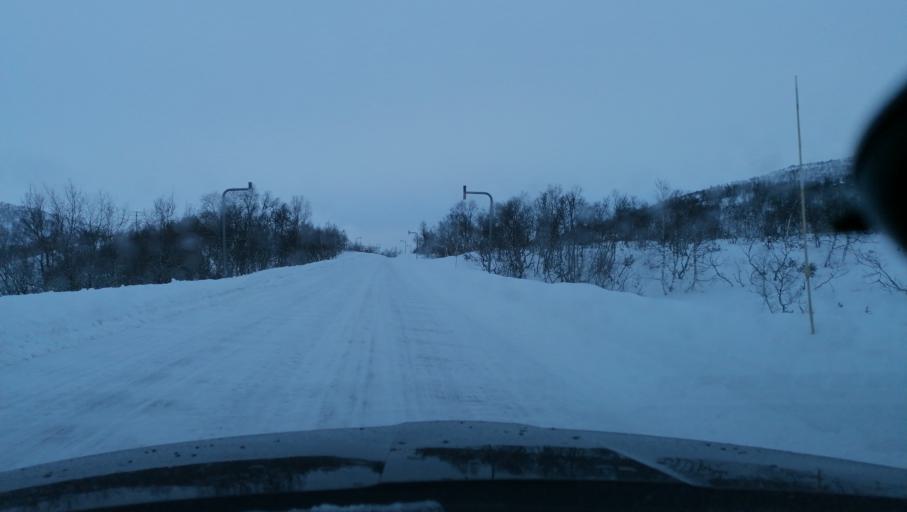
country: NO
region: Aust-Agder
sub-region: Bykle
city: Hovden
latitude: 59.6322
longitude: 7.4537
